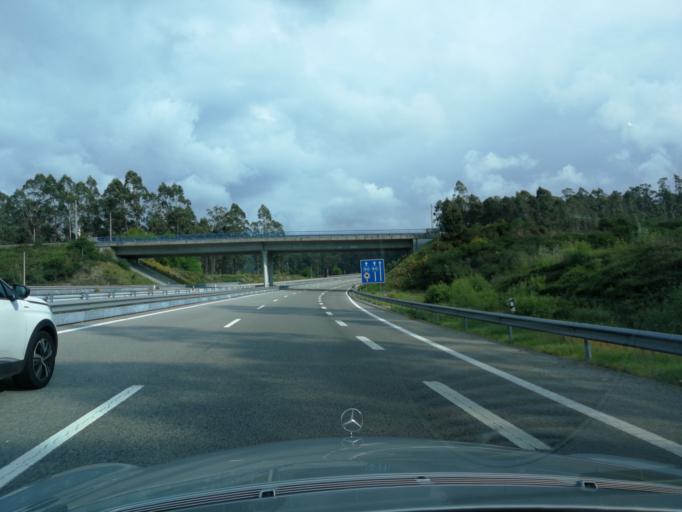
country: PT
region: Porto
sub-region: Vila do Conde
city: Arvore
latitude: 41.3916
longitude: -8.6752
